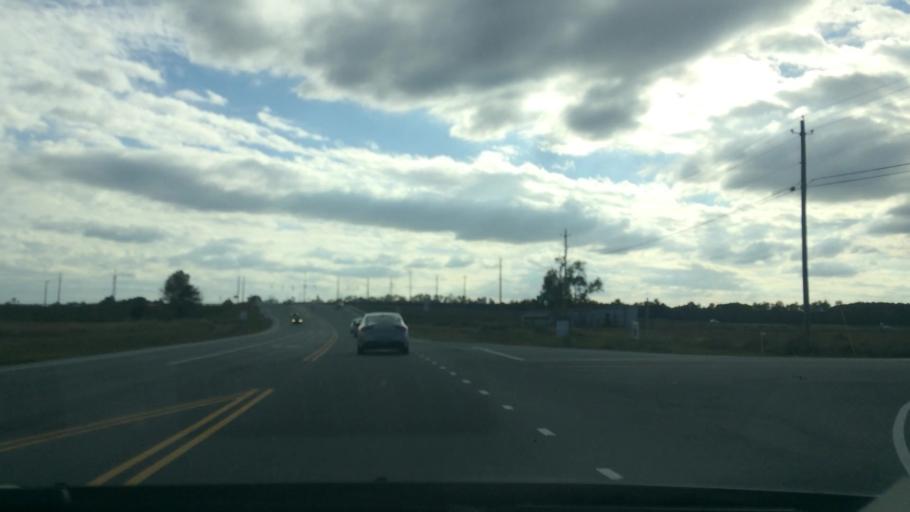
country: US
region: North Carolina
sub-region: Wayne County
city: Elroy
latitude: 35.4159
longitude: -77.8957
